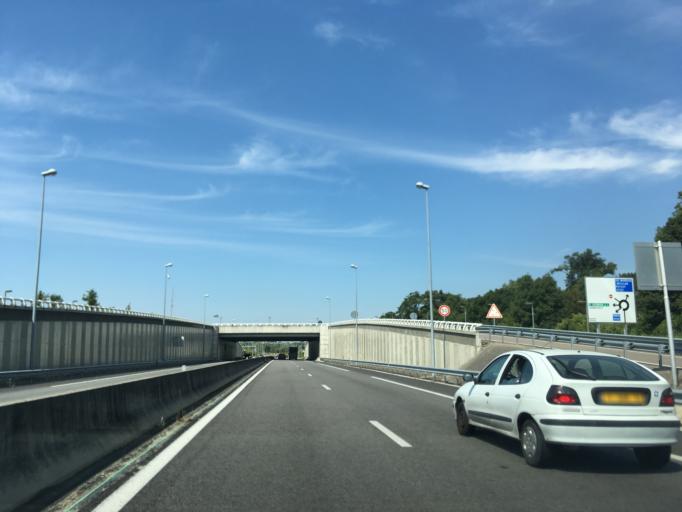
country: FR
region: Ile-de-France
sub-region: Departement des Yvelines
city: Chambourcy
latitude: 48.9087
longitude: 2.0506
